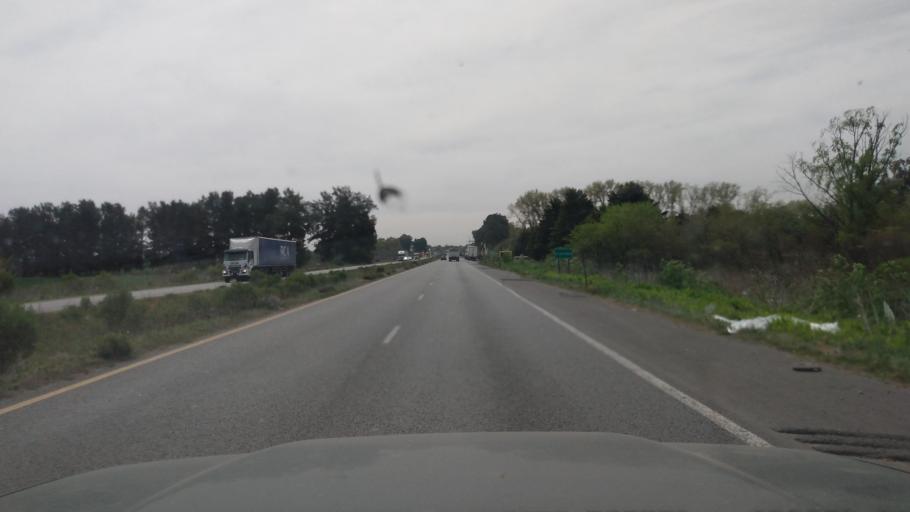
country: AR
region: Buenos Aires
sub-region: Partido de Lujan
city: Lujan
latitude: -34.4615
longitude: -59.0616
